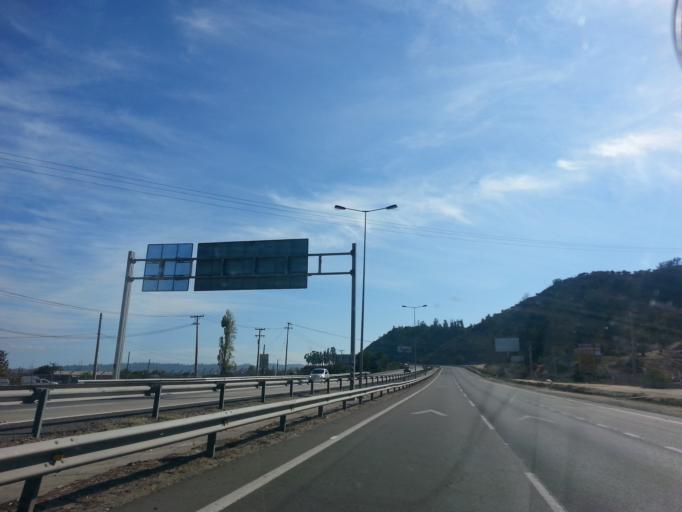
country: CL
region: Valparaiso
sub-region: Provincia de Marga Marga
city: Quilpue
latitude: -33.3265
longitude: -71.3911
